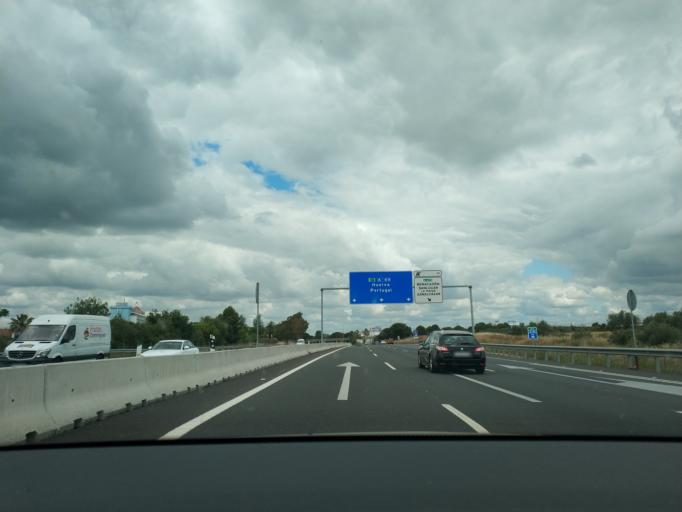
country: ES
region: Andalusia
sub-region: Provincia de Sevilla
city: Benacazon
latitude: 37.3592
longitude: -6.1944
